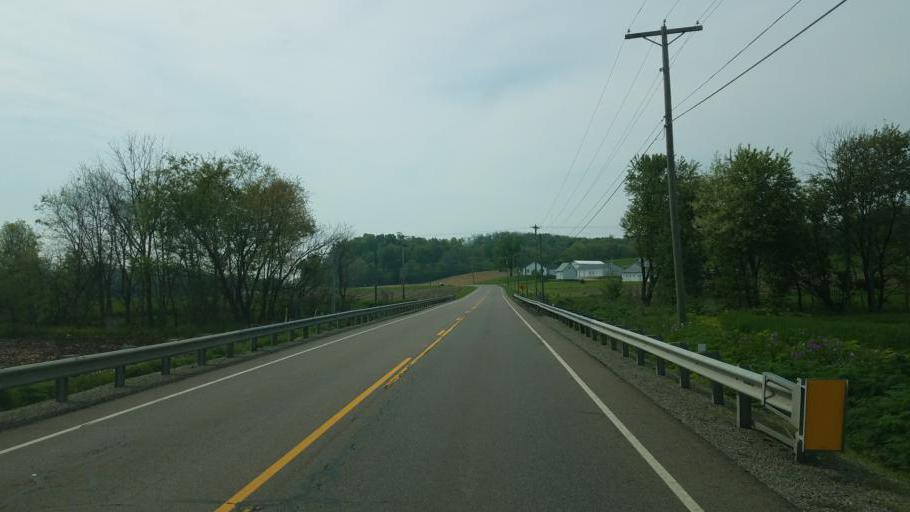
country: US
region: Ohio
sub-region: Licking County
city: Utica
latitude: 40.2248
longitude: -82.4497
